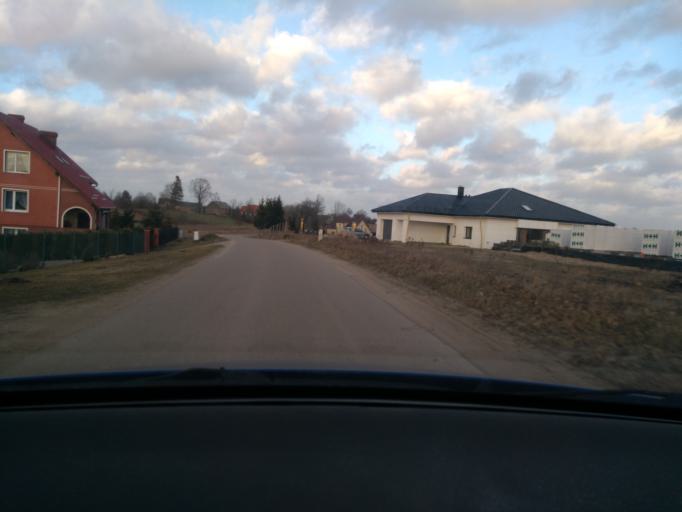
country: PL
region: Pomeranian Voivodeship
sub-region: Powiat kartuski
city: Przodkowo
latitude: 54.4031
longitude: 18.2271
